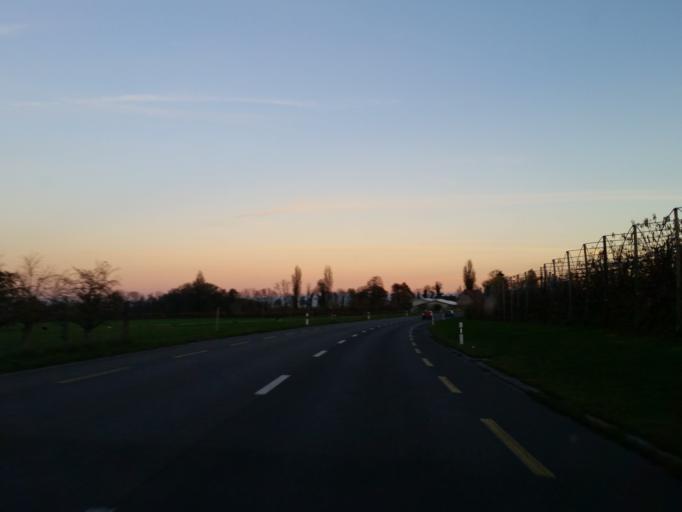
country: CH
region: Thurgau
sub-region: Kreuzlingen District
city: Guttingen
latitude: 47.6017
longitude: 9.2939
